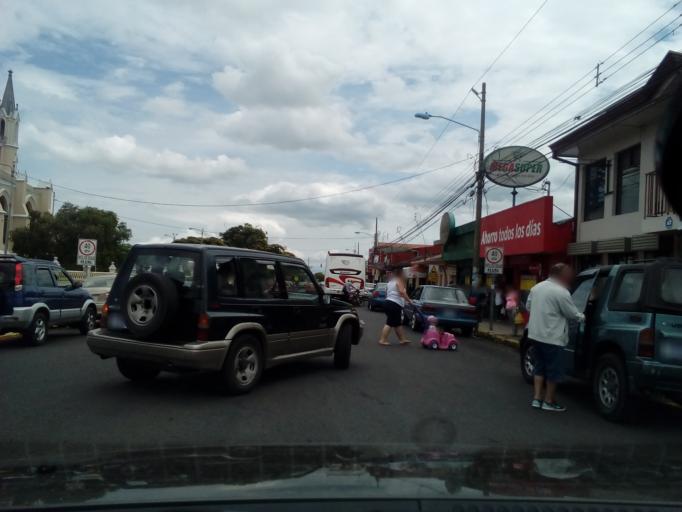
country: CR
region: Heredia
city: San Josecito
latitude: 10.0151
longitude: -84.0983
